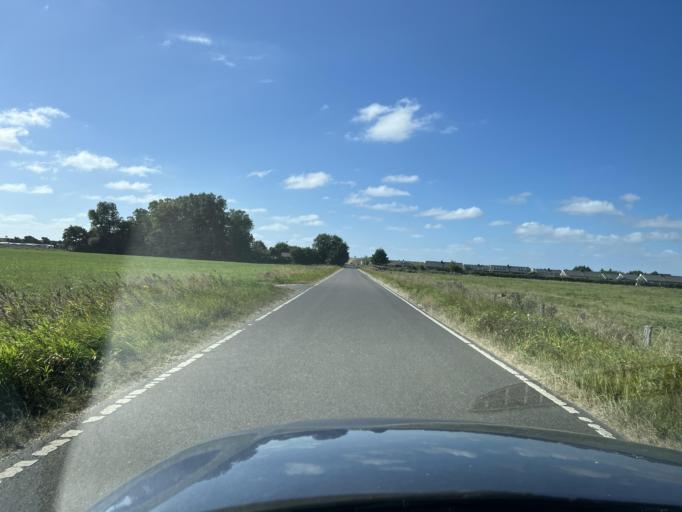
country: DE
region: Schleswig-Holstein
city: Wesselburenerkoog
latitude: 54.2468
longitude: 8.8468
